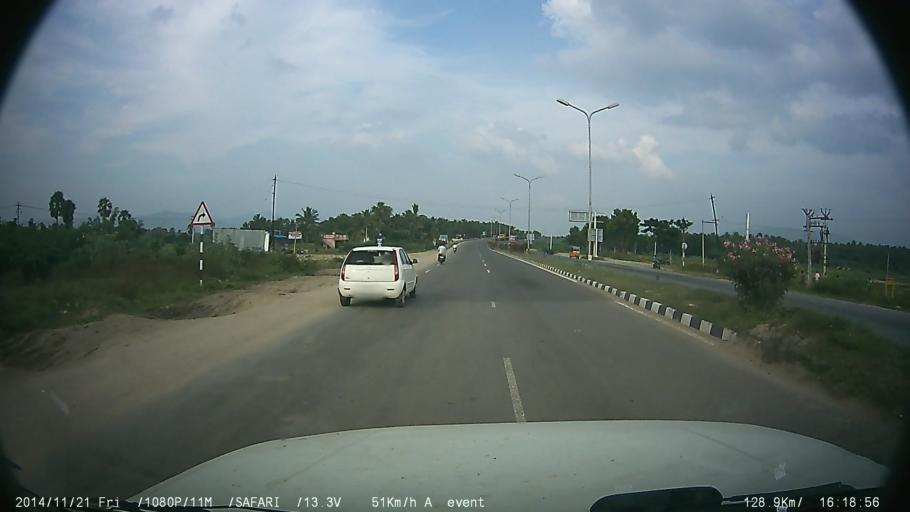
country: IN
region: Tamil Nadu
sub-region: Vellore
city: Vaniyambadi
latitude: 12.6517
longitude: 78.5853
